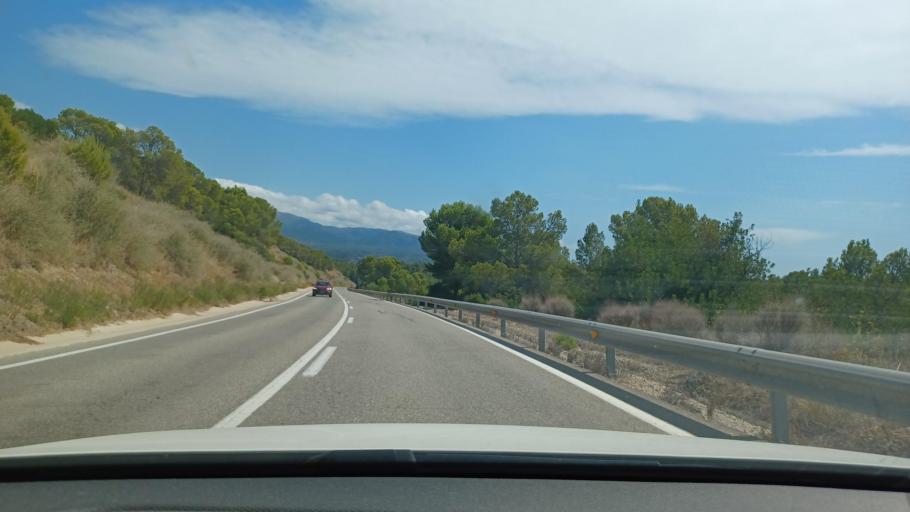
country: ES
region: Catalonia
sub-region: Provincia de Tarragona
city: Tivenys
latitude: 40.9379
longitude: 0.4682
